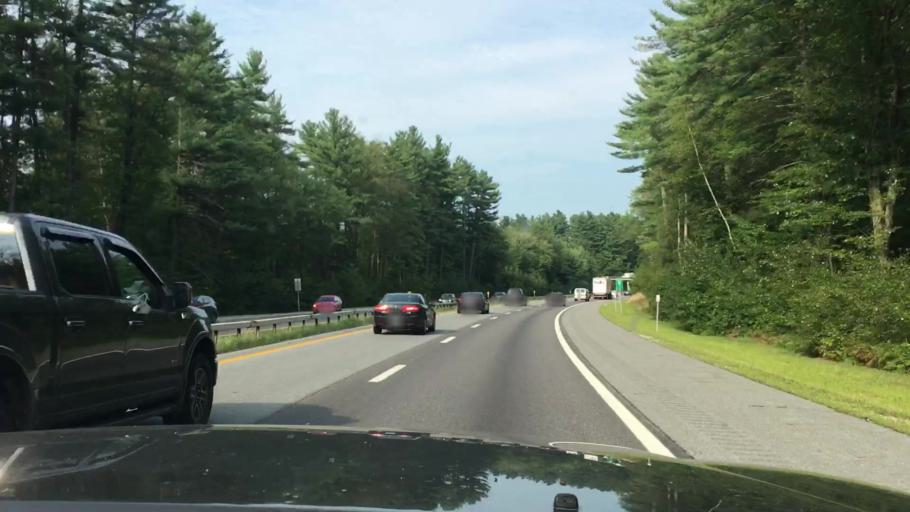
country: US
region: New Hampshire
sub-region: Hillsborough County
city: Merrimack
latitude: 42.8725
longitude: -71.4992
